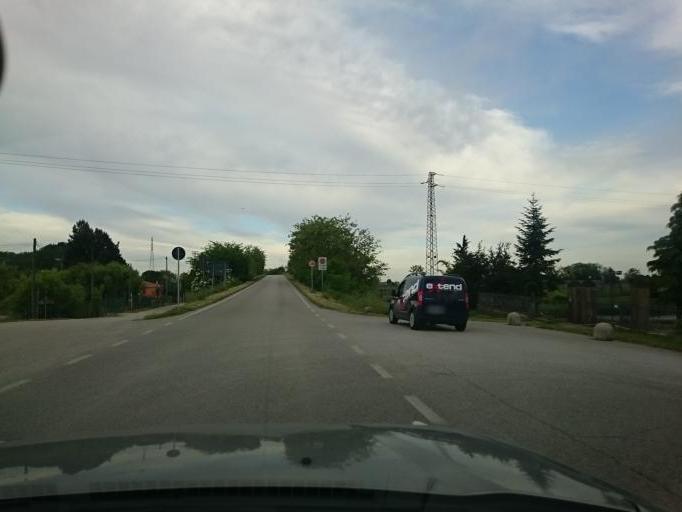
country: IT
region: Veneto
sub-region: Provincia di Padova
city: Monselice
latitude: 45.2376
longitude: 11.7716
